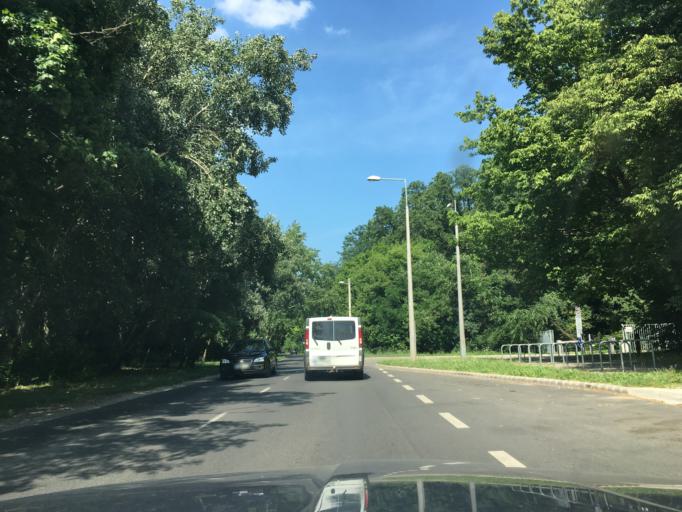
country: HU
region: Hajdu-Bihar
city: Debrecen
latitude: 47.5572
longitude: 21.6162
